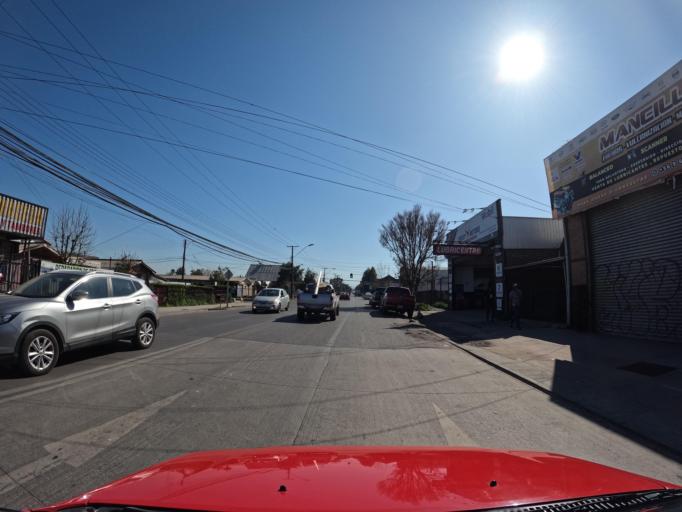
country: CL
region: Maule
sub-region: Provincia de Curico
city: Curico
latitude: -34.9757
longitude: -71.2482
